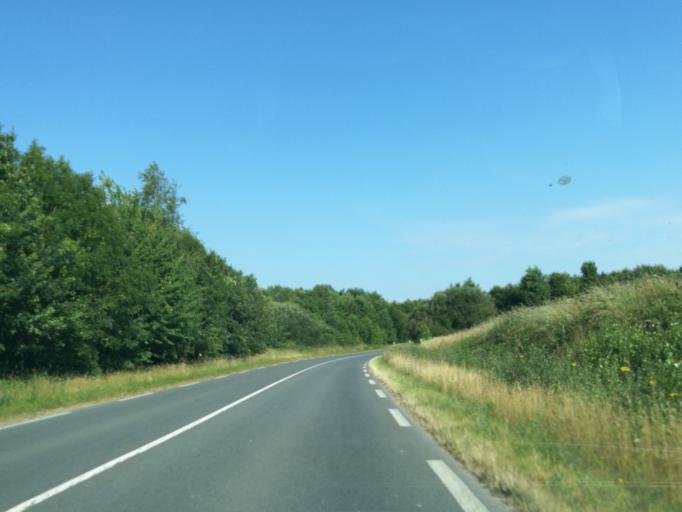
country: FR
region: Brittany
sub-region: Departement d'Ille-et-Vilaine
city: Montfort-sur-Meu
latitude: 48.1483
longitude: -1.9443
